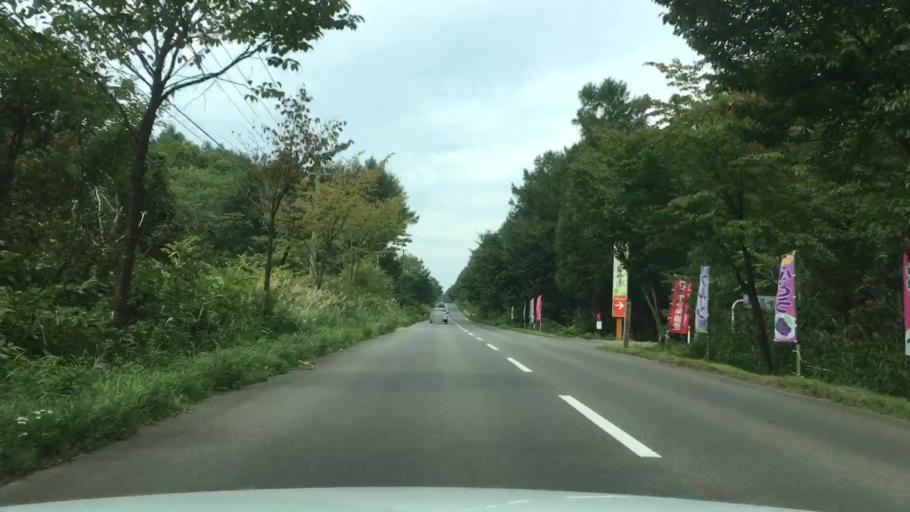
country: JP
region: Aomori
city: Shimokizukuri
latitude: 40.7110
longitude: 140.3316
